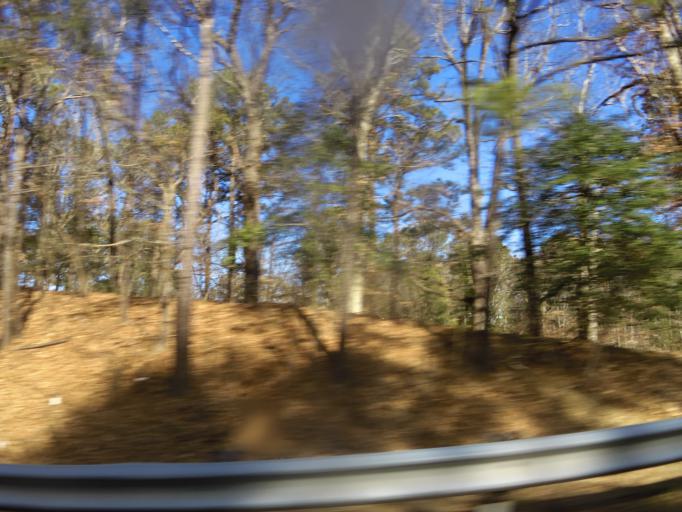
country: US
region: Virginia
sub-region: Isle of Wight County
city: Smithfield
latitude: 36.9644
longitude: -76.6114
